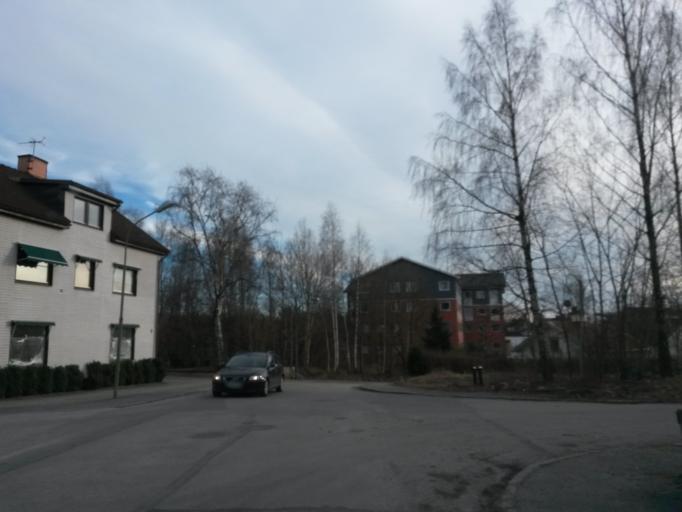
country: SE
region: Vaestra Goetaland
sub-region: Boras Kommun
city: Boras
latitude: 57.7353
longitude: 12.9404
